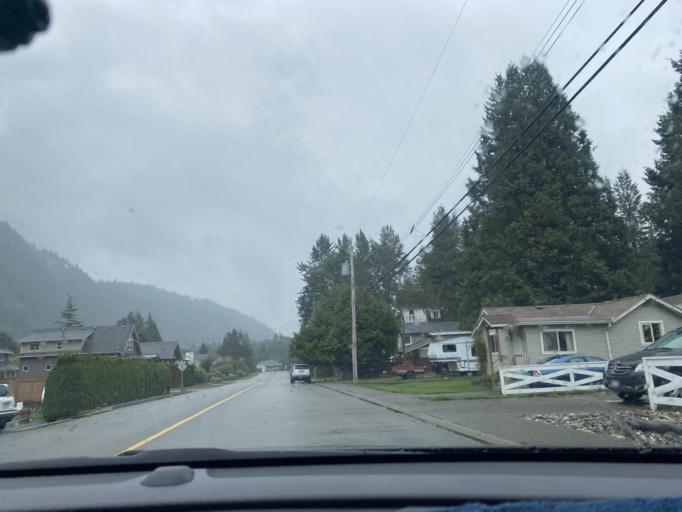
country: CA
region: British Columbia
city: Agassiz
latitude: 49.3017
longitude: -121.7782
